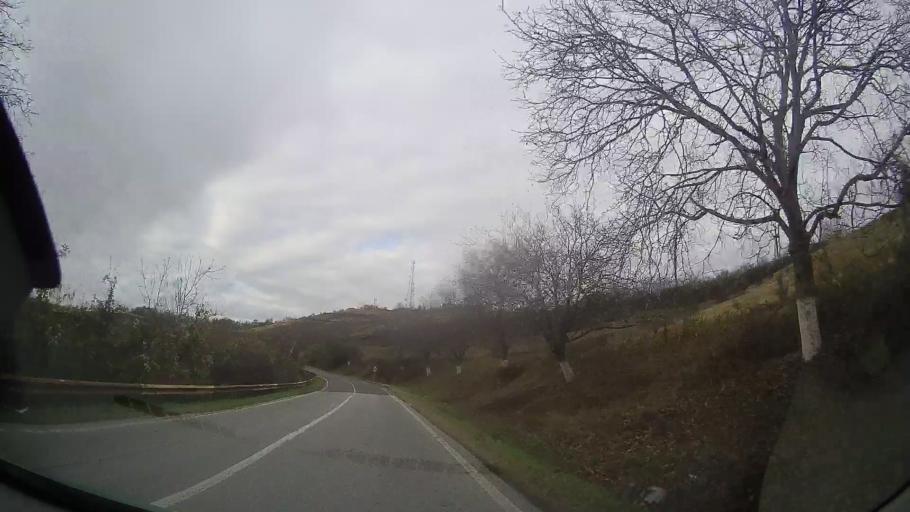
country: RO
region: Bistrita-Nasaud
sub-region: Comuna Silvasu de Campie
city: Silvasu de Campie
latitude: 46.7763
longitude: 24.3232
